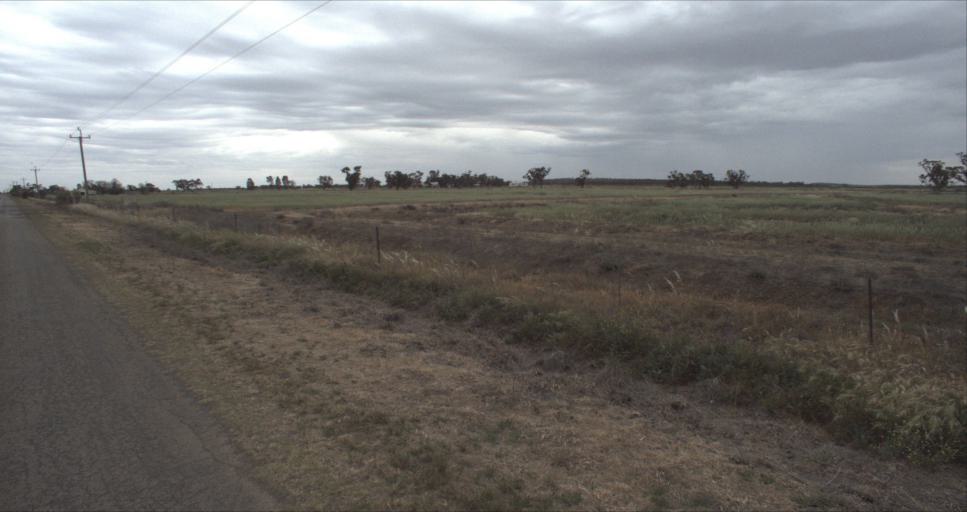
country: AU
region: New South Wales
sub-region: Leeton
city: Leeton
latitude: -34.4095
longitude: 146.3406
